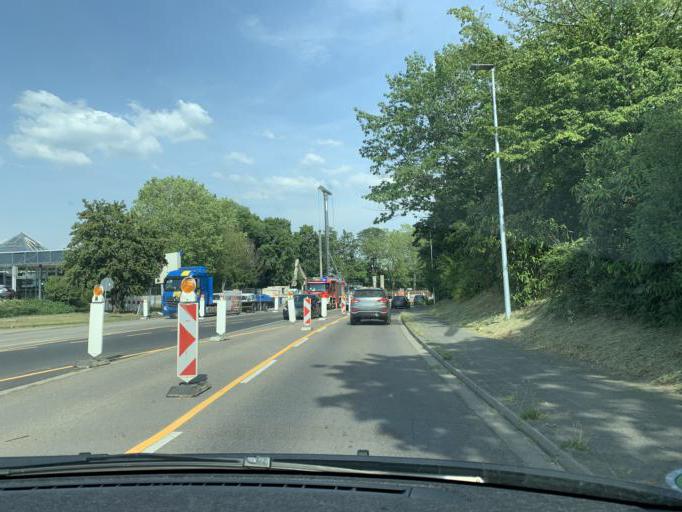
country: DE
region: North Rhine-Westphalia
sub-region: Regierungsbezirk Dusseldorf
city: Viersen
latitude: 51.2620
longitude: 6.3916
